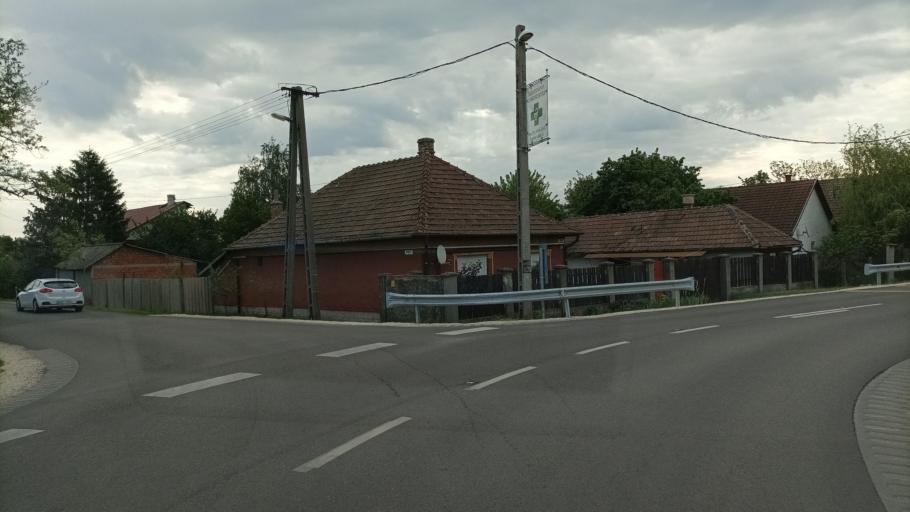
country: HU
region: Pest
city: Pilis
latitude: 47.2847
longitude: 19.5315
